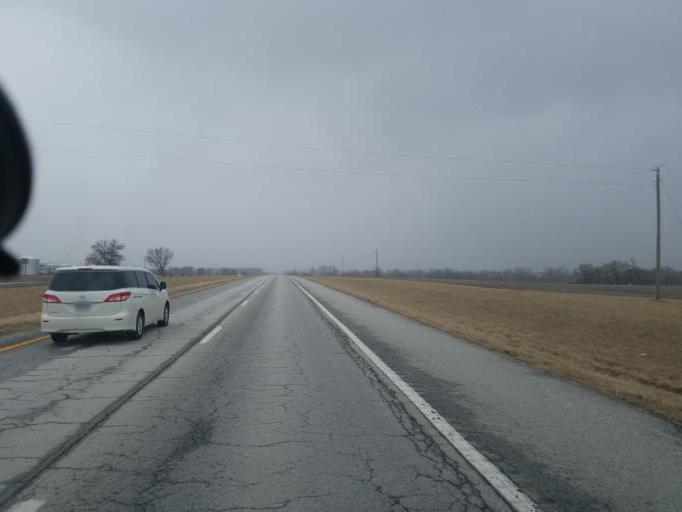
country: US
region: Missouri
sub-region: Macon County
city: La Plata
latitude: 40.0084
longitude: -92.4753
